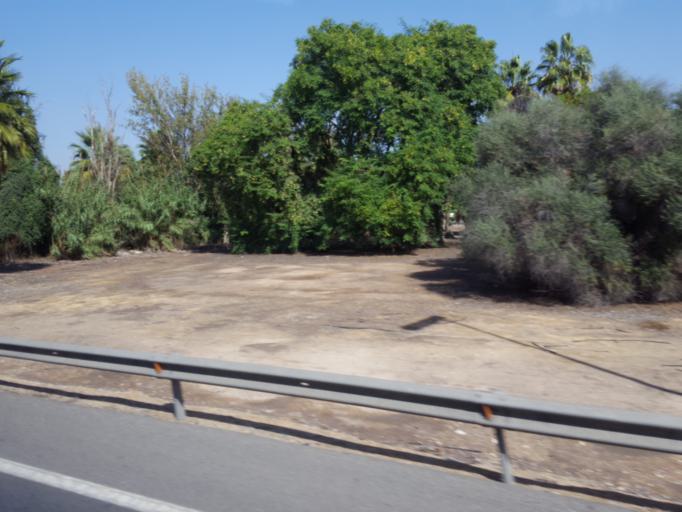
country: ES
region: Murcia
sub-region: Murcia
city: Murcia
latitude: 37.9978
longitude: -1.1513
